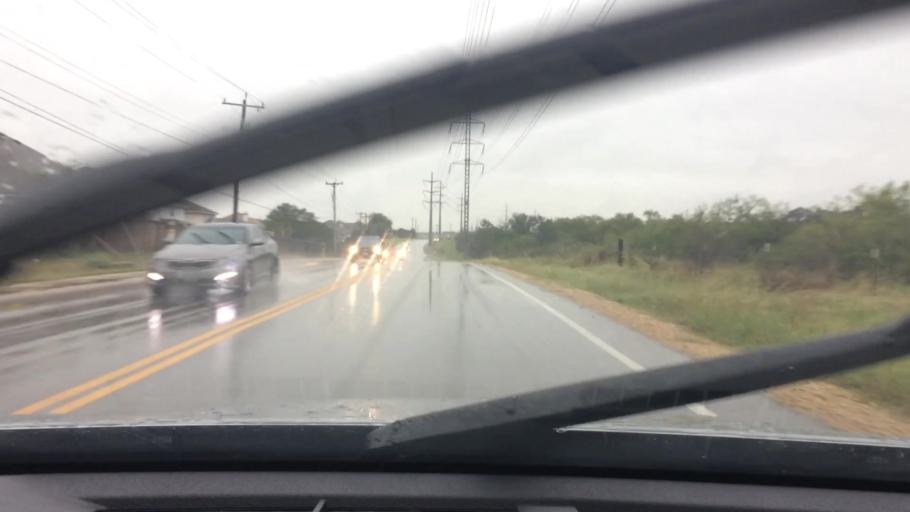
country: US
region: Texas
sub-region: Bexar County
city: Kirby
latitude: 29.4658
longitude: -98.3483
